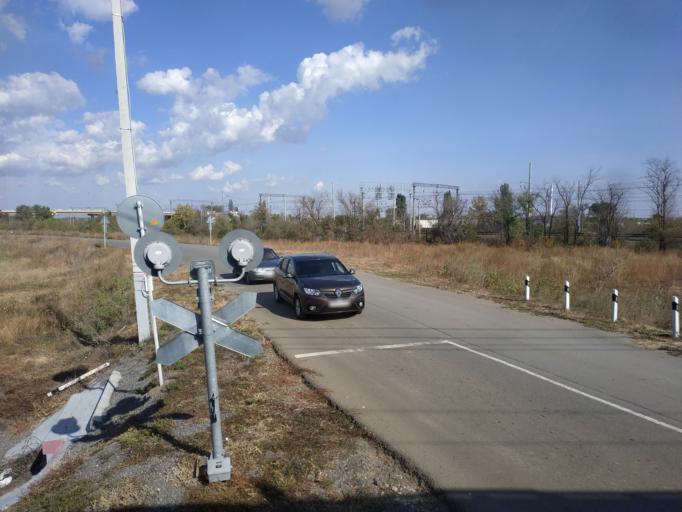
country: RU
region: Volgograd
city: Gumrak
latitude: 48.7938
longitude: 44.3632
